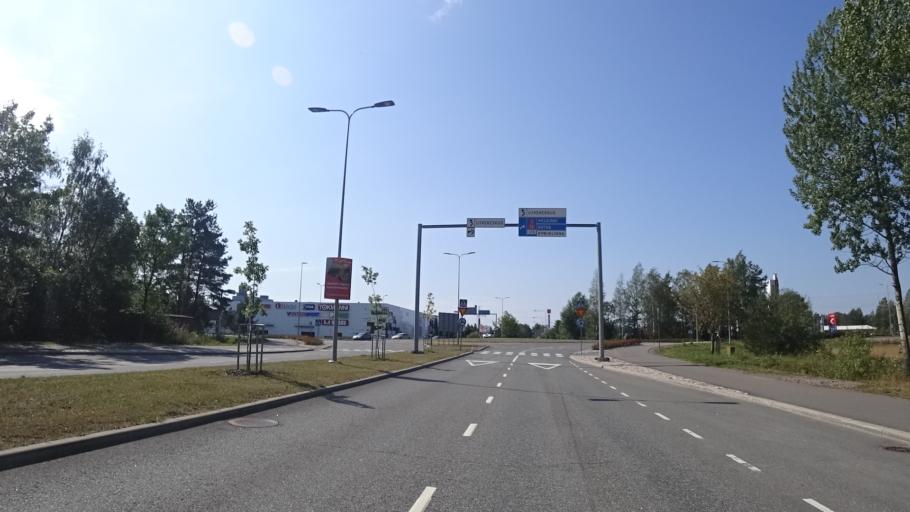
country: FI
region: Kymenlaakso
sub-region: Kotka-Hamina
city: Karhula
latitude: 60.5072
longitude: 26.9189
